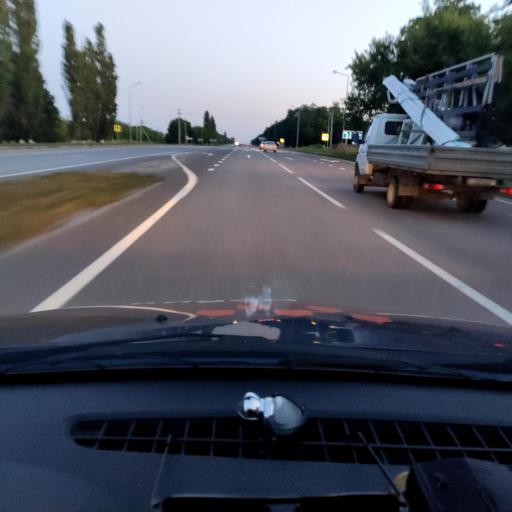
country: RU
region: Belgorod
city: Bekhteyevka
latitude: 50.8564
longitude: 37.1758
